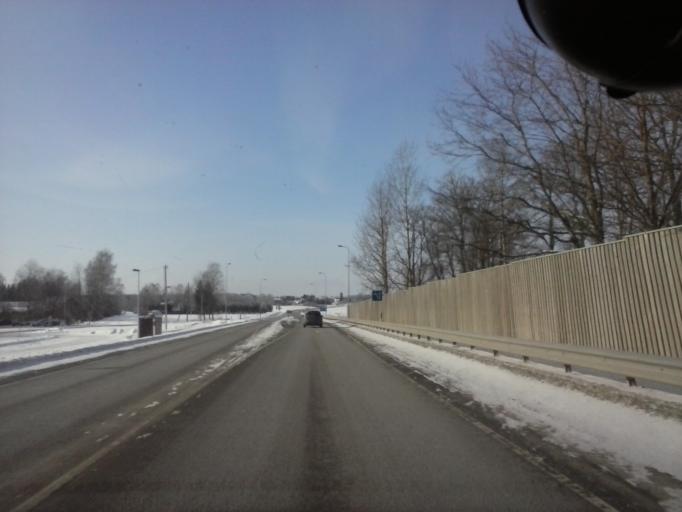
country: EE
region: Tartu
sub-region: Tartu linn
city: Tartu
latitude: 58.3569
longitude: 26.6204
